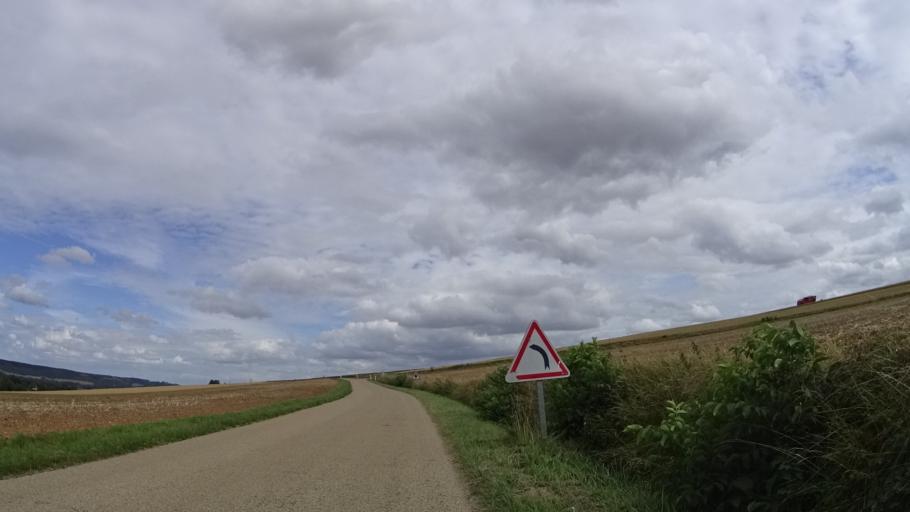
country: FR
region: Bourgogne
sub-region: Departement de l'Yonne
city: Cezy
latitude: 47.9819
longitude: 3.2976
